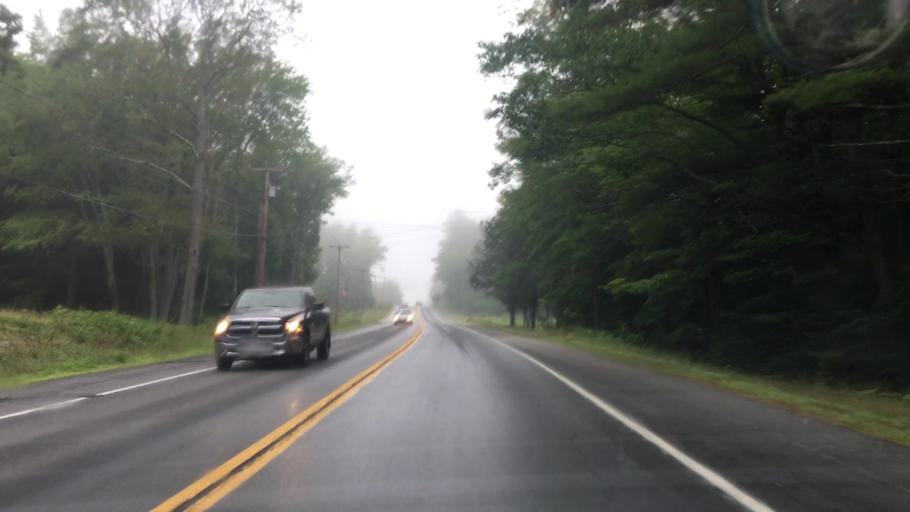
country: US
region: Maine
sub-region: Lincoln County
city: Wiscasset
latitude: 43.9829
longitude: -69.6996
